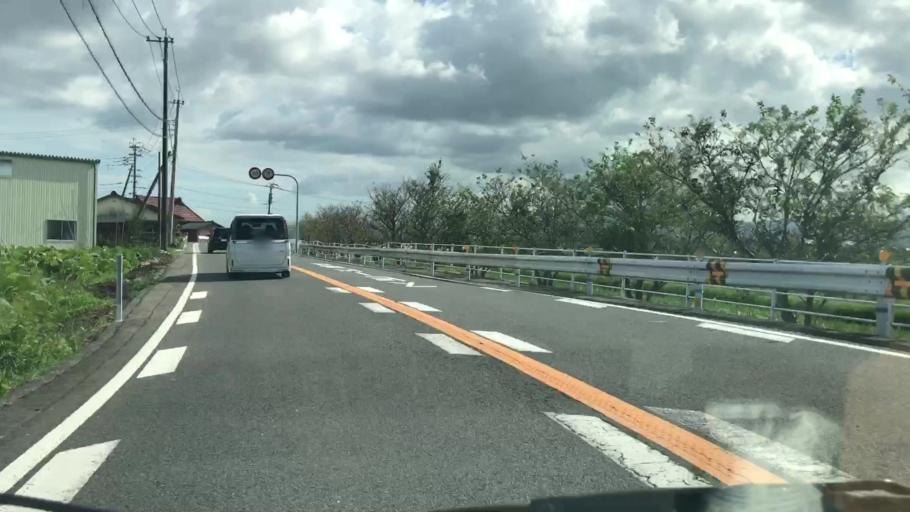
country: JP
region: Saga Prefecture
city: Kashima
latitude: 33.1642
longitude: 130.1682
